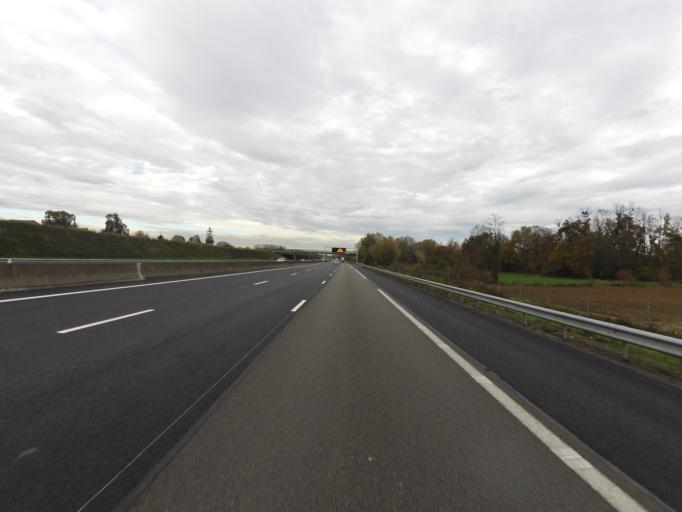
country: FR
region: Rhone-Alpes
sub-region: Departement du Rhone
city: Saint-Georges-de-Reneins
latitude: 46.0738
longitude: 4.7416
